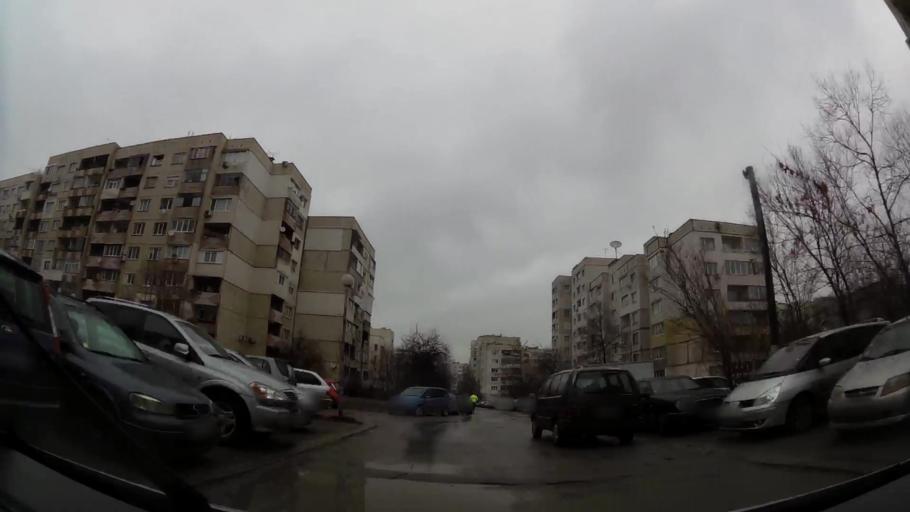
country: BG
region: Sofia-Capital
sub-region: Stolichna Obshtina
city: Sofia
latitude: 42.6282
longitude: 23.3765
